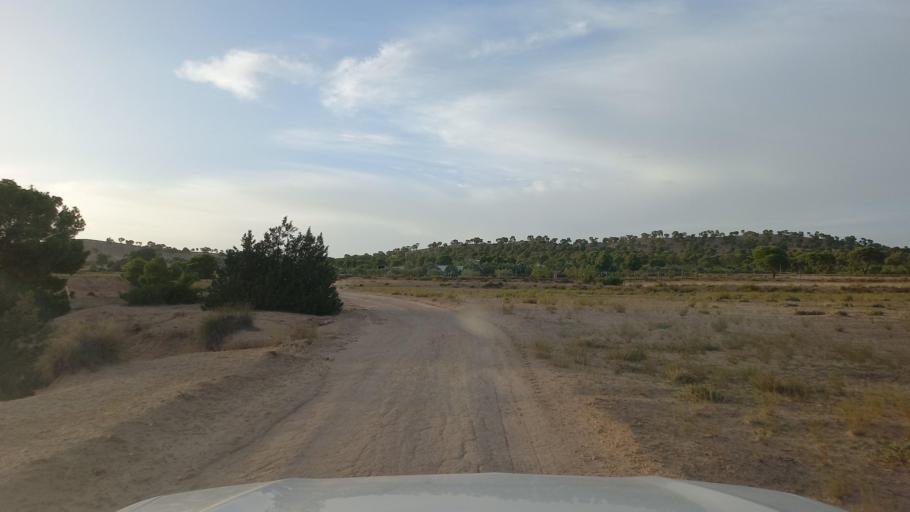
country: TN
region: Al Qasrayn
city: Sbiba
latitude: 35.4107
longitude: 8.9148
